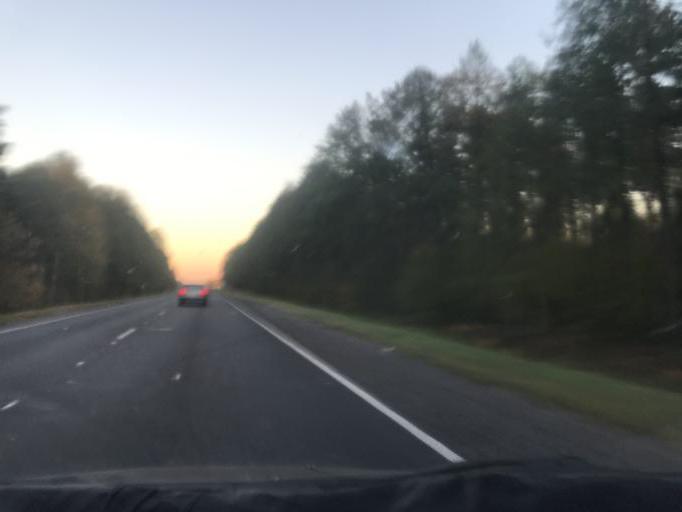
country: BY
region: Gomel
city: Kalinkavichy
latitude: 52.1707
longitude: 29.2042
